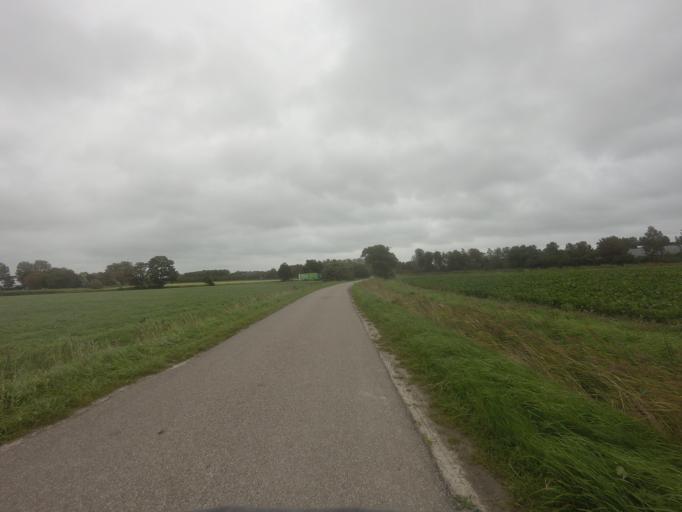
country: NL
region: Friesland
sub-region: Gemeente Leeuwarderadeel
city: Stiens
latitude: 53.2696
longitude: 5.7522
